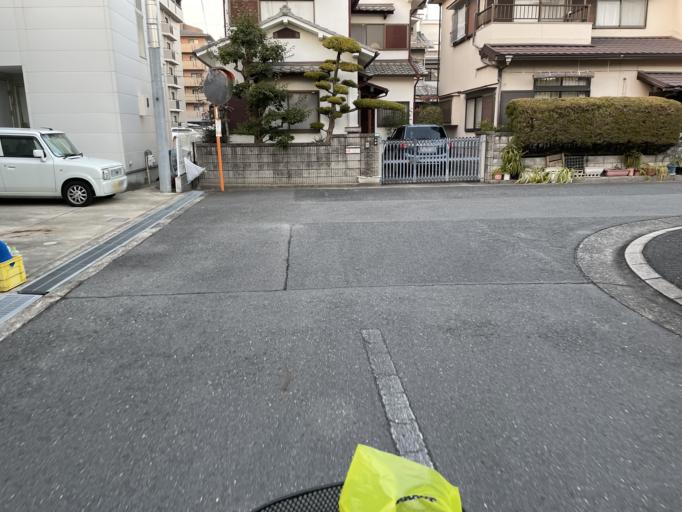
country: JP
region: Osaka
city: Ibaraki
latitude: 34.8027
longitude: 135.5843
